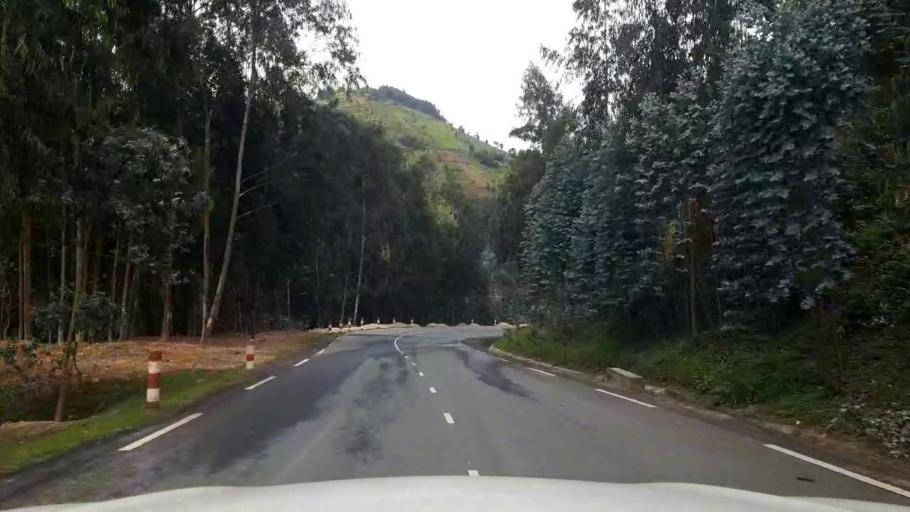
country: RW
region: Northern Province
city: Musanze
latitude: -1.6847
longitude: 29.5286
